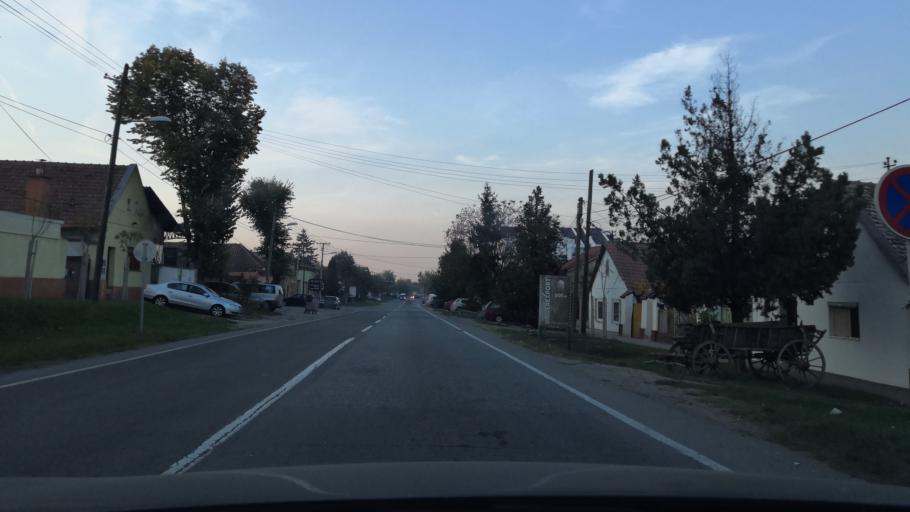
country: RS
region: Autonomna Pokrajina Vojvodina
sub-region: Juznobacki Okrug
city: Petrovaradin
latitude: 45.2375
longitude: 19.8844
